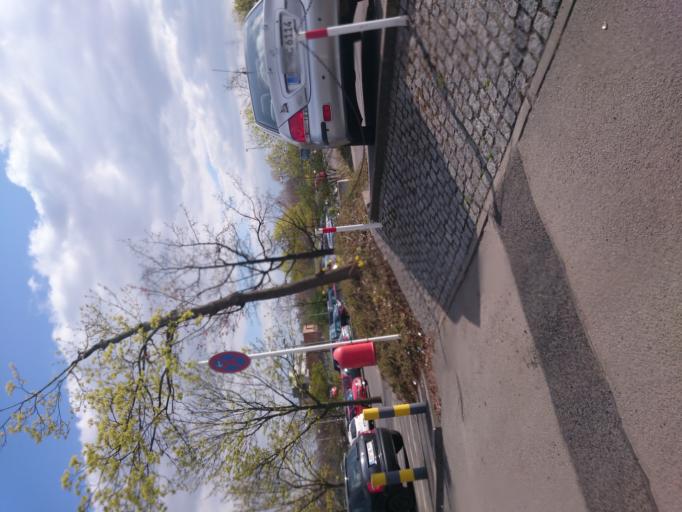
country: DE
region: Berlin
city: Charlottenburg-Nord
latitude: 52.5526
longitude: 13.2959
